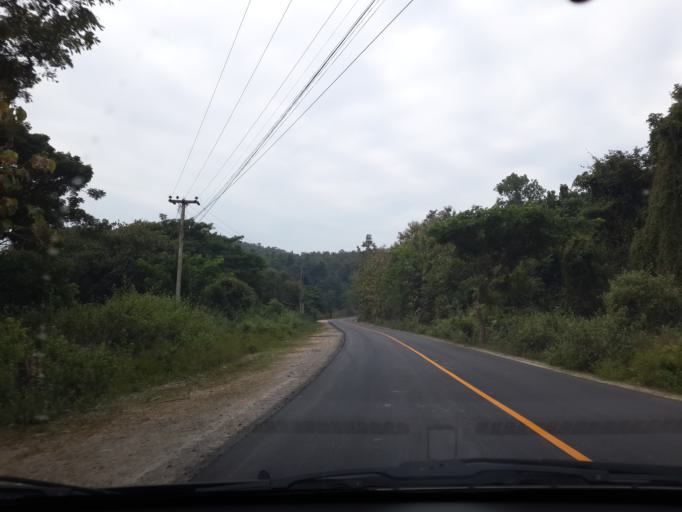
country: TH
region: Chiang Mai
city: San Sai
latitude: 18.9208
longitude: 99.1226
